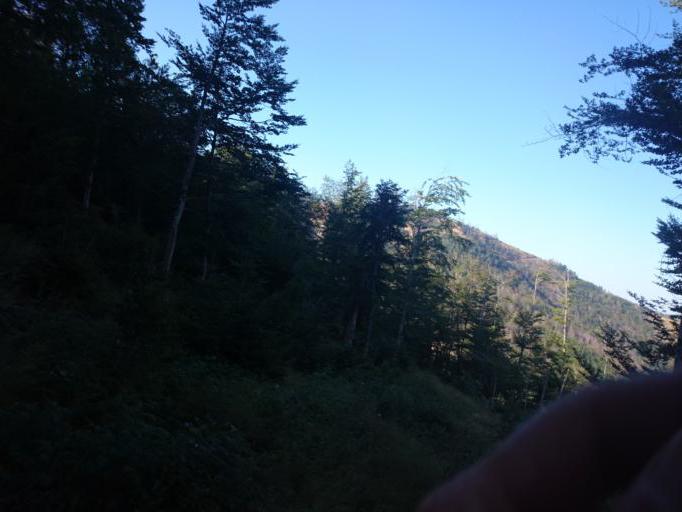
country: AL
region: Diber
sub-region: Rrethi i Bulqizes
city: Martanesh
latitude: 41.4049
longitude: 20.3021
